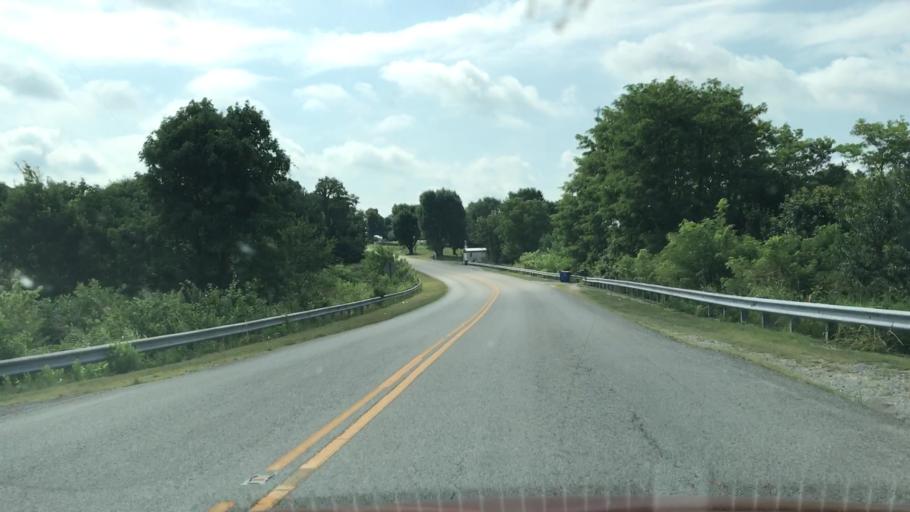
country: US
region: Kentucky
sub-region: Barren County
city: Glasgow
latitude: 36.9781
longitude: -85.8991
